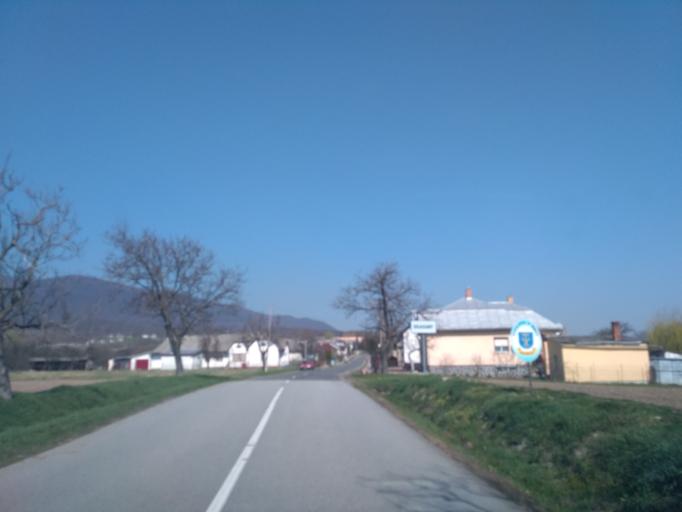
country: SK
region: Kosicky
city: Secovce
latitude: 48.7552
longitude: 21.6433
